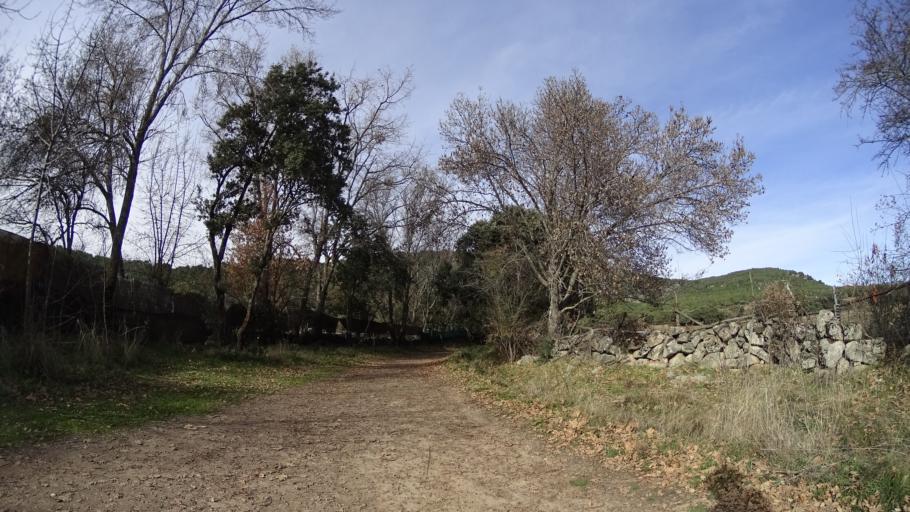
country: ES
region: Madrid
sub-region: Provincia de Madrid
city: Moralzarzal
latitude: 40.6675
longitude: -3.9865
